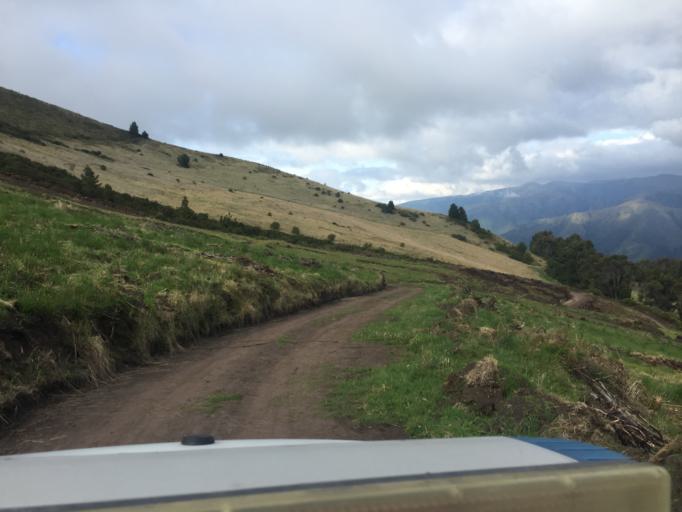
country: EC
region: Imbabura
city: Ibarra
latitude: 0.2263
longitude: -78.1222
